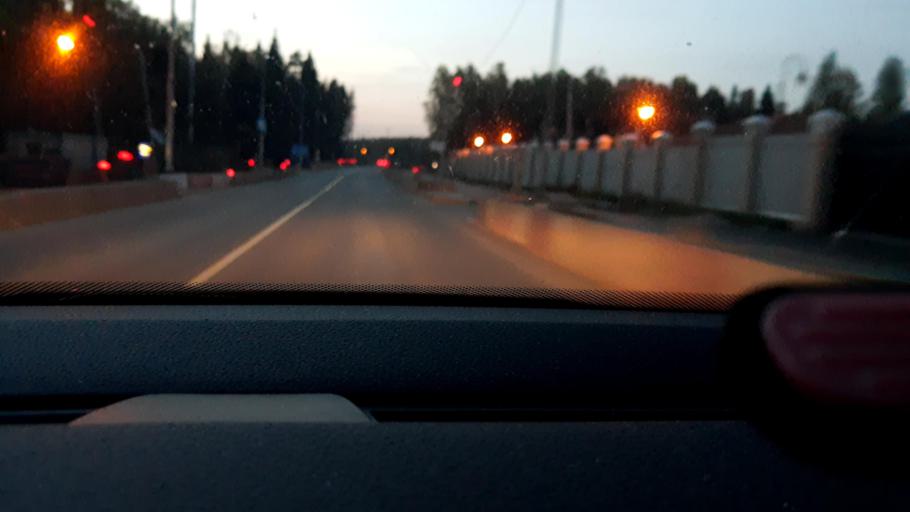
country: RU
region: Moskovskaya
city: Filimonki
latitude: 55.5486
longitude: 37.3542
